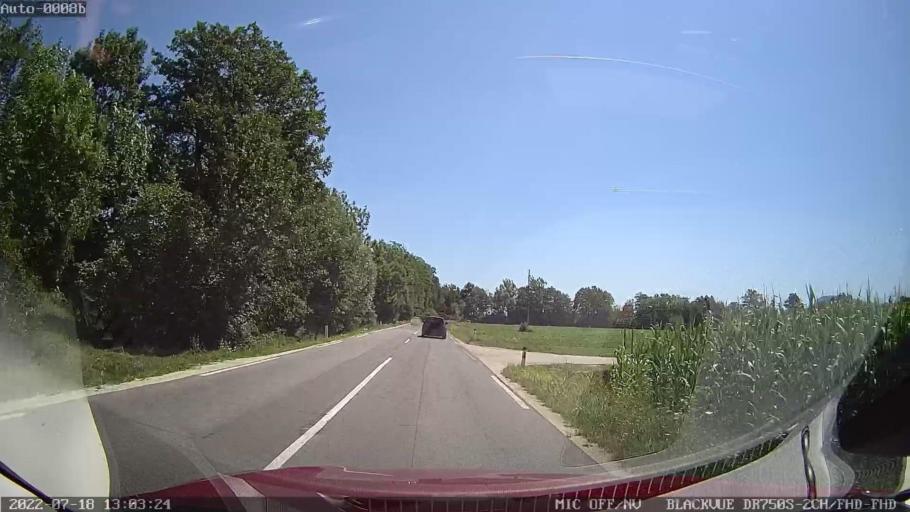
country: SI
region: Brezovica
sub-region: Opstina Ljubljana-Vic-Rudnik
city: Brezovica pri Ljubljani
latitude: 46.0505
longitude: 14.4323
